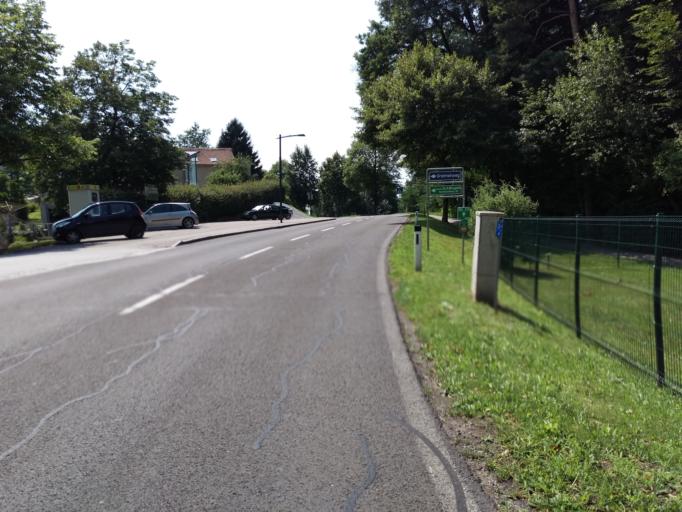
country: AT
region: Styria
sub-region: Politischer Bezirk Graz-Umgebung
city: Nestelbach bei Graz
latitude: 47.0736
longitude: 15.5920
